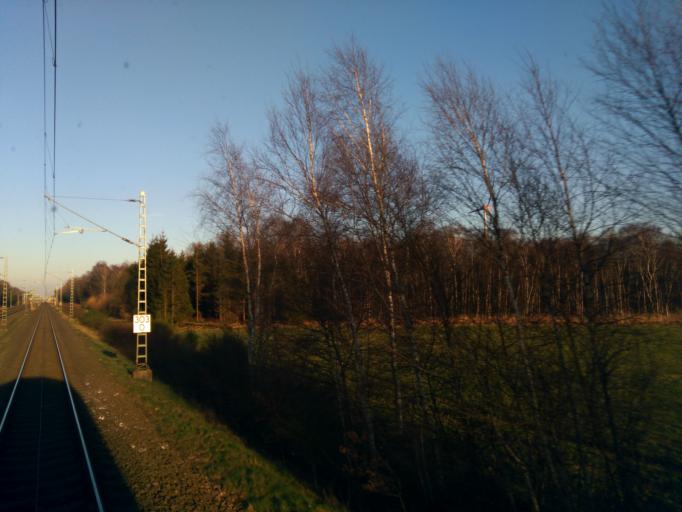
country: DE
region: Lower Saxony
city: Vahlde
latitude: 53.2243
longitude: 9.6291
